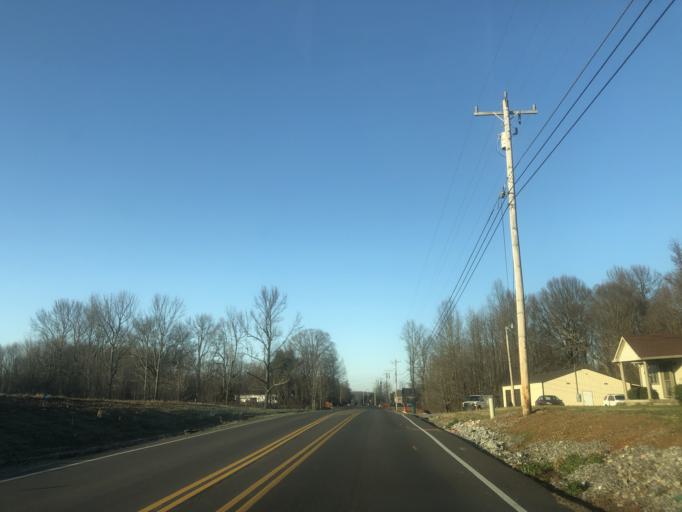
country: US
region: Tennessee
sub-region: Sumner County
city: White House
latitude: 36.4791
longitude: -86.6933
